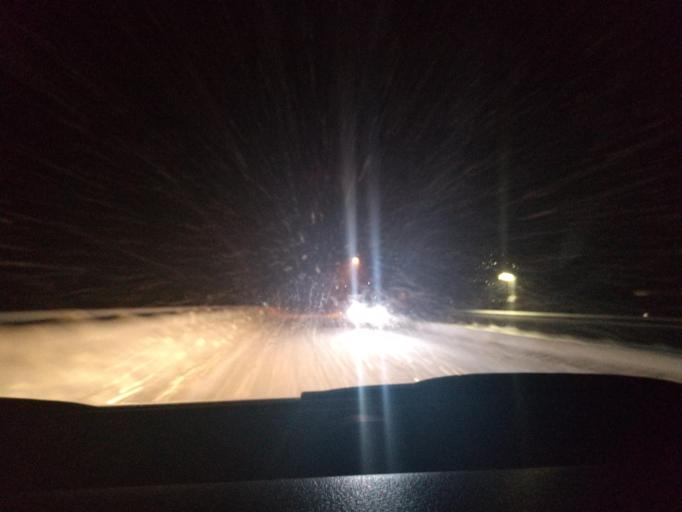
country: JP
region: Akita
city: Kakunodatemachi
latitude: 39.6063
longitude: 140.6224
